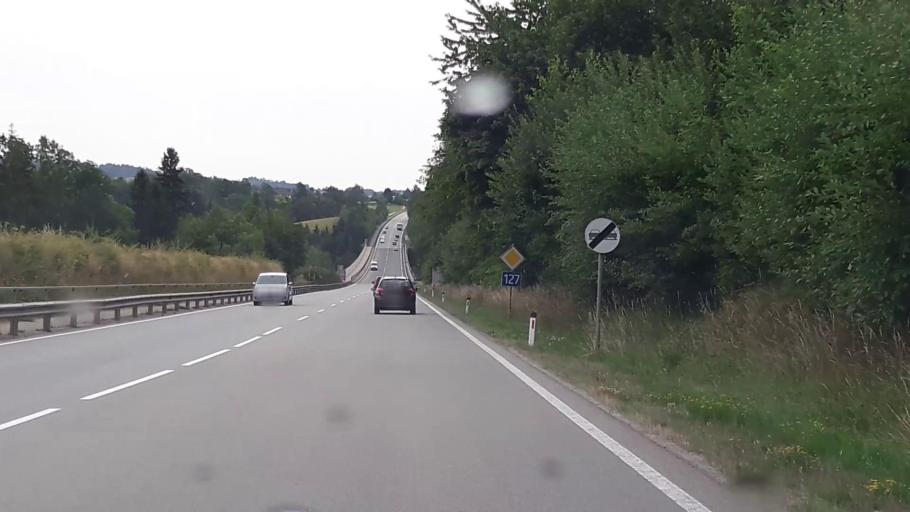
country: AT
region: Upper Austria
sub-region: Politischer Bezirk Rohrbach
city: Kleinzell im Muehlkreis
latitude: 48.4795
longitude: 13.9903
